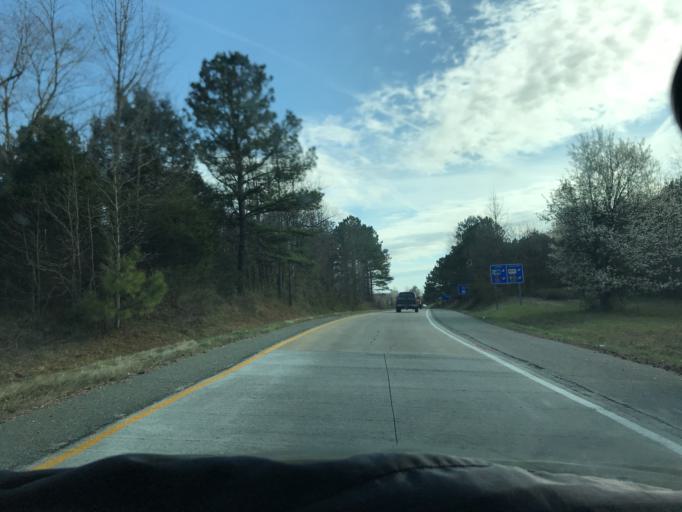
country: US
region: Virginia
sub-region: Chesterfield County
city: Brandermill
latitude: 37.4261
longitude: -77.6321
